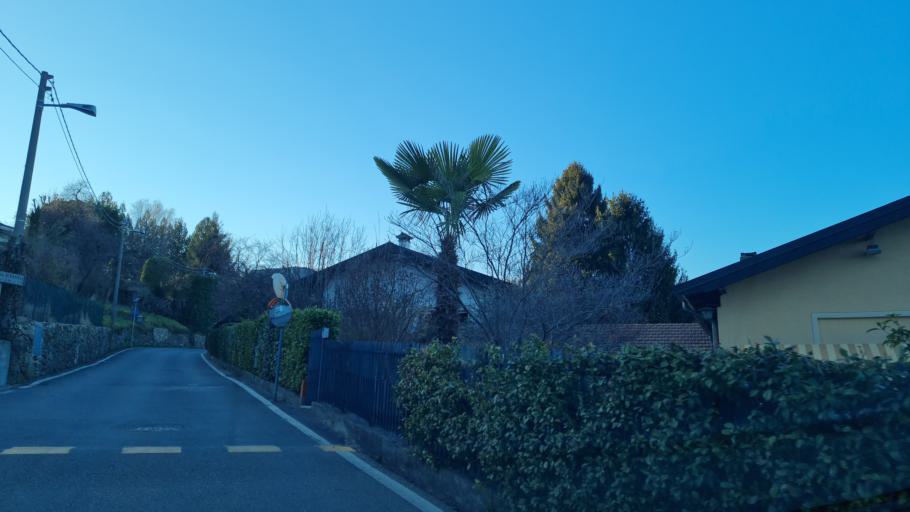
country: IT
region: Piedmont
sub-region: Provincia di Novara
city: Meina
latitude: 45.7889
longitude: 8.5303
